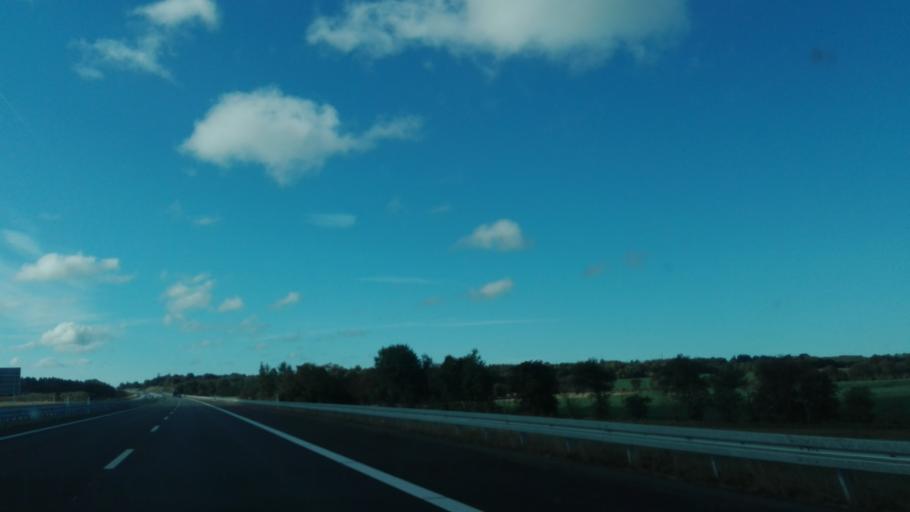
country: DK
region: Central Jutland
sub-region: Silkeborg Kommune
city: Silkeborg
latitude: 56.1883
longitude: 9.4925
